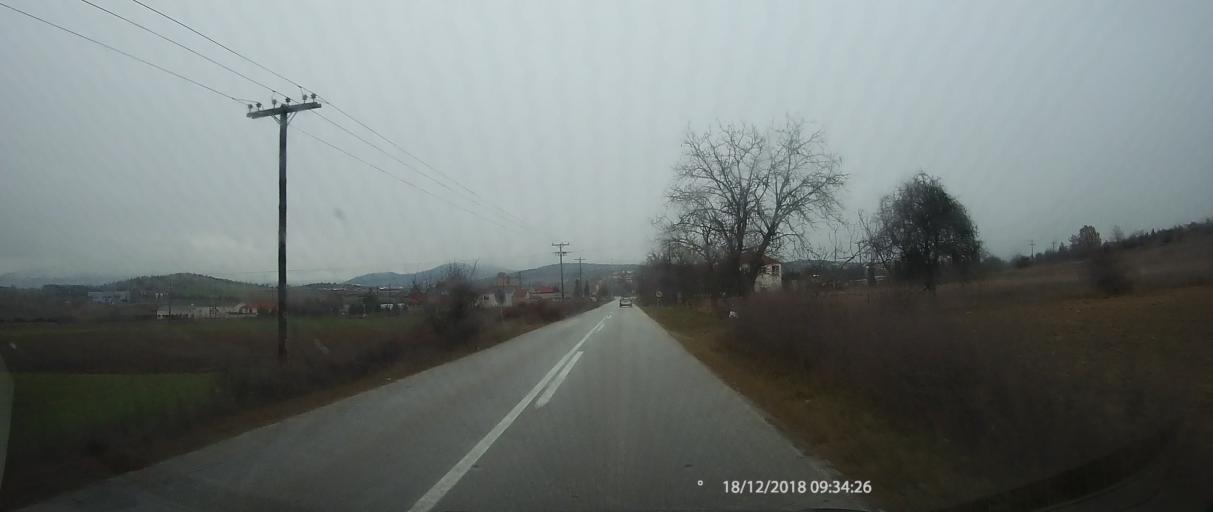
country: GR
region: Thessaly
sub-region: Nomos Larisis
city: Elassona
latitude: 39.9731
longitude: 22.1822
